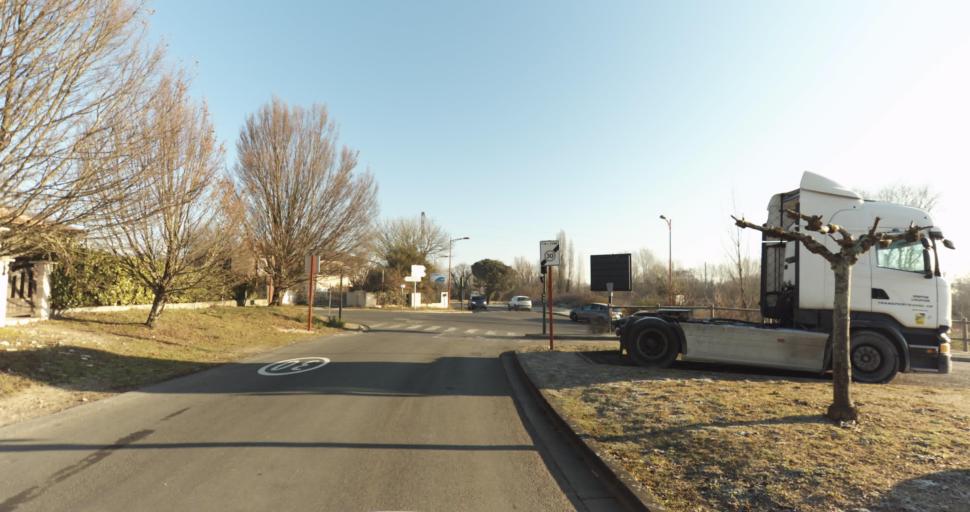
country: FR
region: Aquitaine
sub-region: Departement de la Gironde
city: Carbon-Blanc
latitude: 44.9030
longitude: -0.4975
